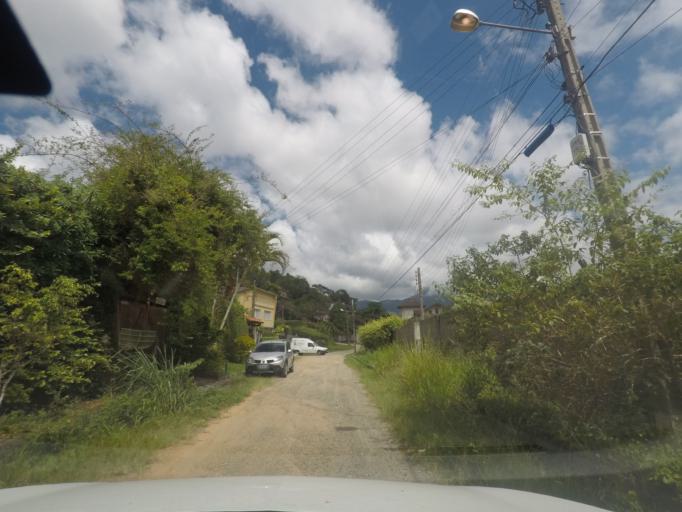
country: BR
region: Rio de Janeiro
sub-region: Teresopolis
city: Teresopolis
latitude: -22.3991
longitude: -42.9845
